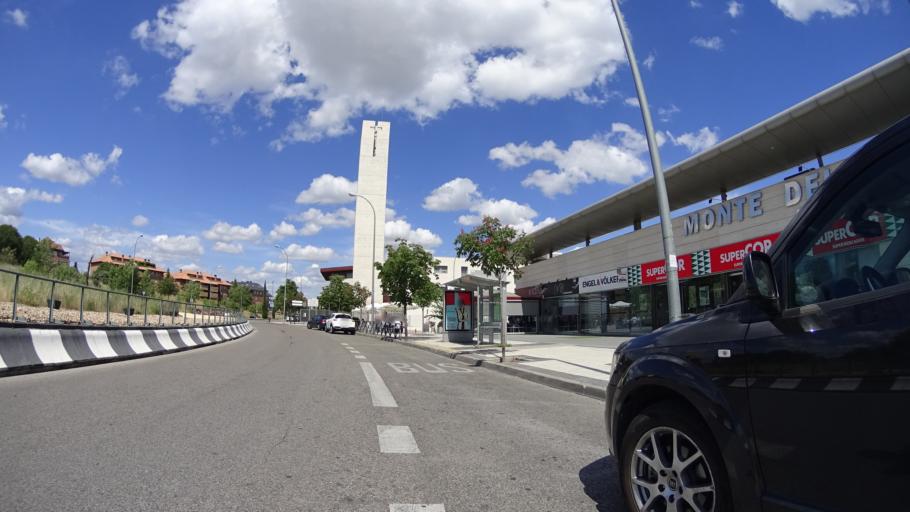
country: ES
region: Madrid
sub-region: Provincia de Madrid
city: Majadahonda
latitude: 40.4693
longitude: -3.8540
